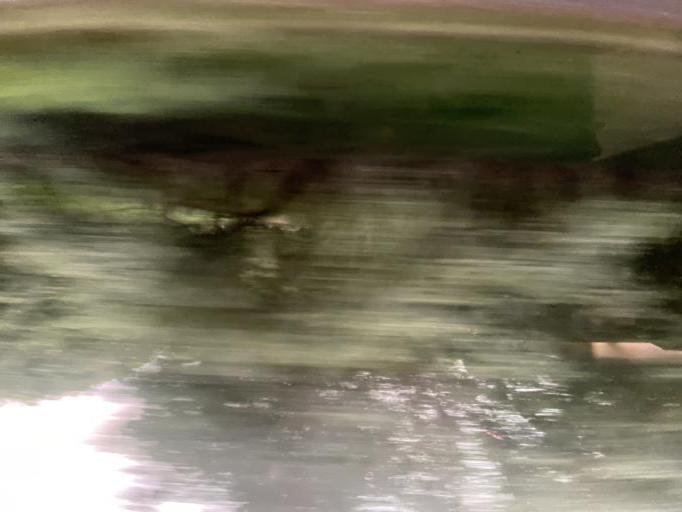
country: US
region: West Virginia
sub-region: Mineral County
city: Fort Ashby
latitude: 39.5203
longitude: -78.5701
